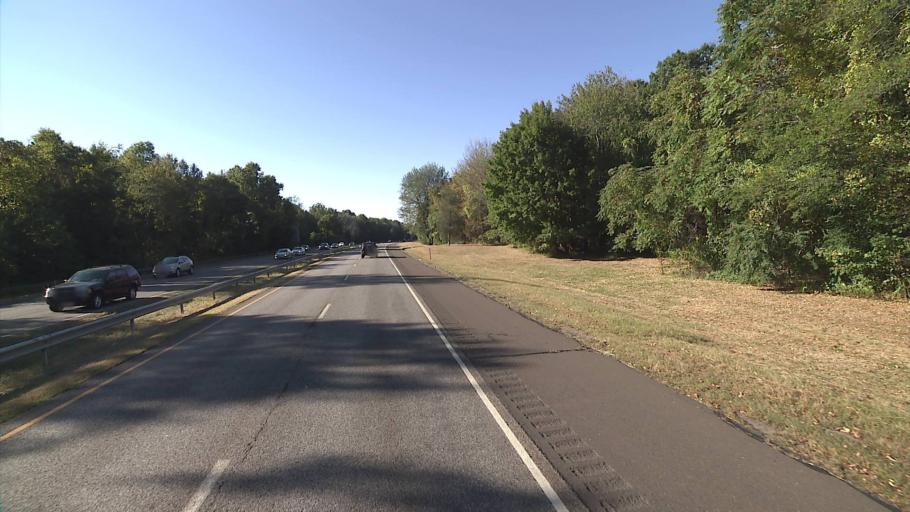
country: US
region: Connecticut
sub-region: New Haven County
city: Wallingford
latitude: 41.4490
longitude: -72.8422
